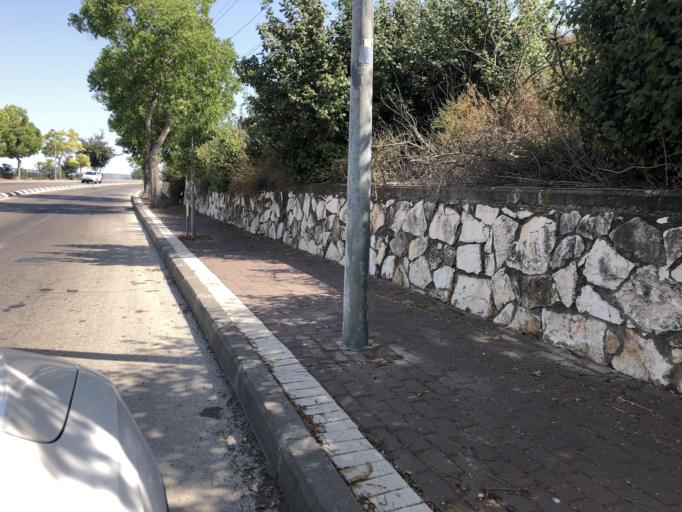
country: IL
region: Haifa
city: Daliyat el Karmil
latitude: 32.6404
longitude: 35.0925
